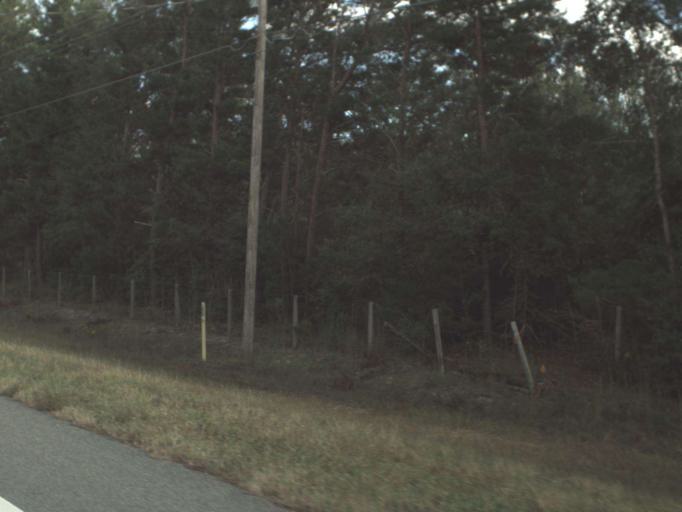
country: US
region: Florida
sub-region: Walton County
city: DeFuniak Springs
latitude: 30.7661
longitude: -86.1120
